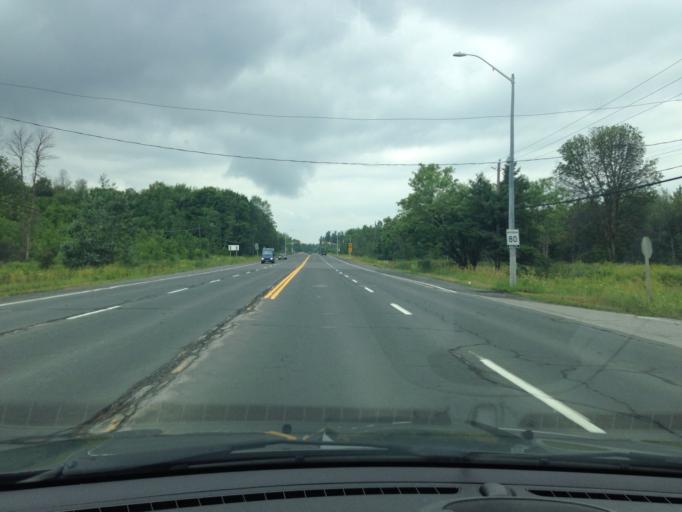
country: CA
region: Ontario
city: Ottawa
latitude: 45.3383
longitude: -75.6079
